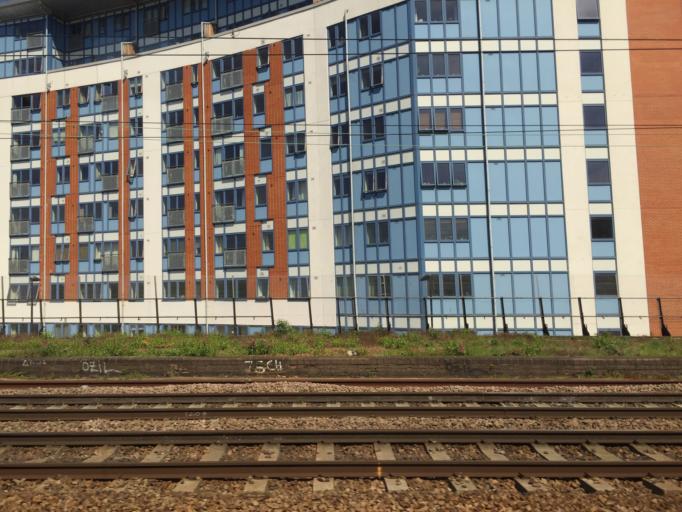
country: GB
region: England
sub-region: Greater London
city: Bethnal Green
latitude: 51.5271
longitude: -0.0419
